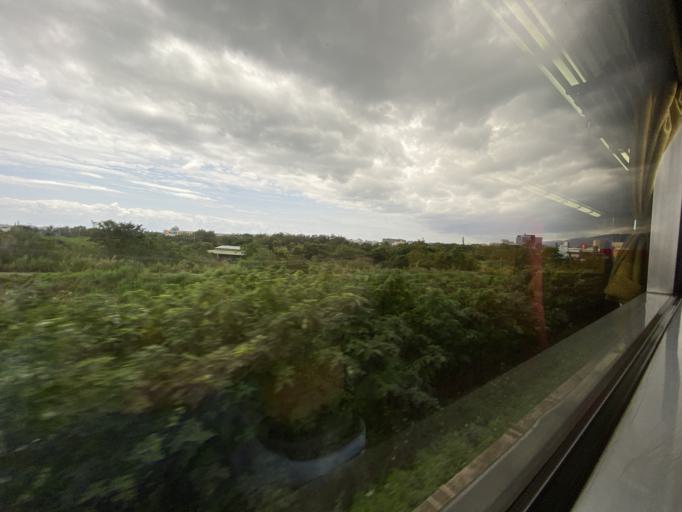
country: TW
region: Taiwan
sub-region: Taitung
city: Taitung
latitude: 22.7759
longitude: 121.1093
